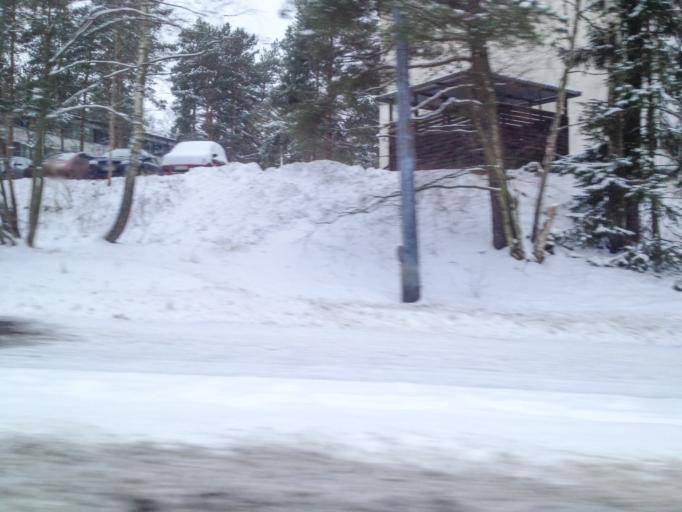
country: FI
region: Uusimaa
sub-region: Helsinki
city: Vantaa
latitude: 60.2217
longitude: 25.1338
